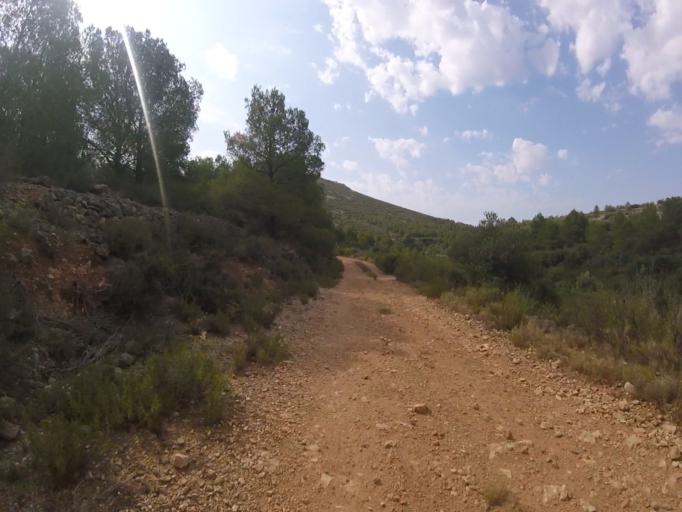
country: ES
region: Valencia
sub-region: Provincia de Castello
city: Alcala de Xivert
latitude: 40.3556
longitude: 0.1993
